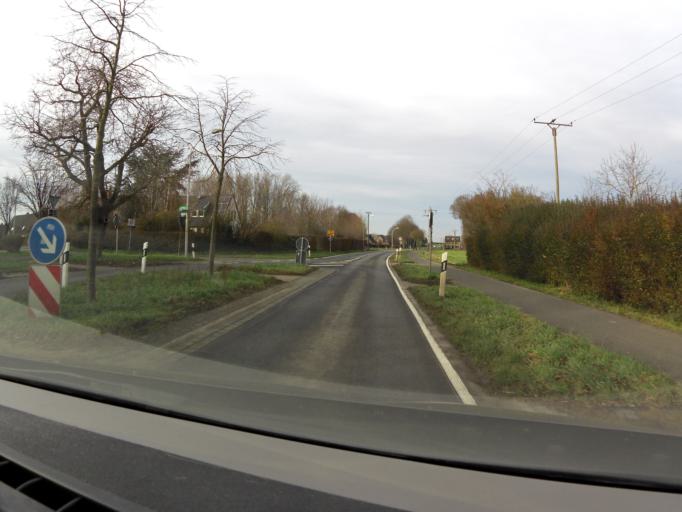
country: DE
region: North Rhine-Westphalia
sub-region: Regierungsbezirk Dusseldorf
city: Nettetal
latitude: 51.3083
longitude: 6.2424
